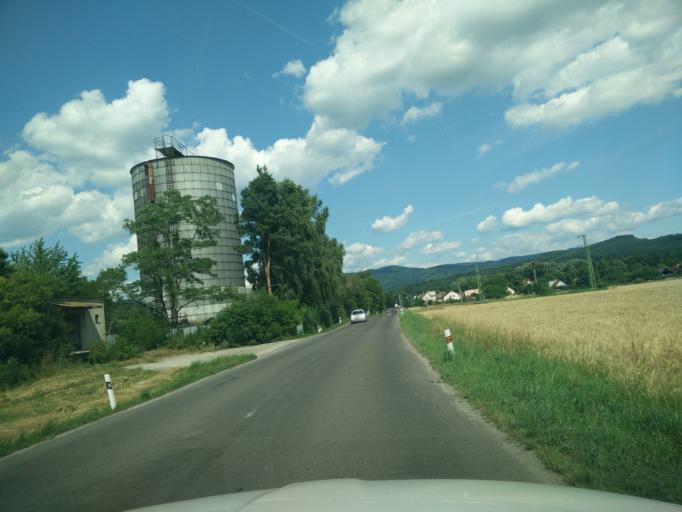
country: SK
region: Nitriansky
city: Prievidza
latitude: 48.8175
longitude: 18.6366
